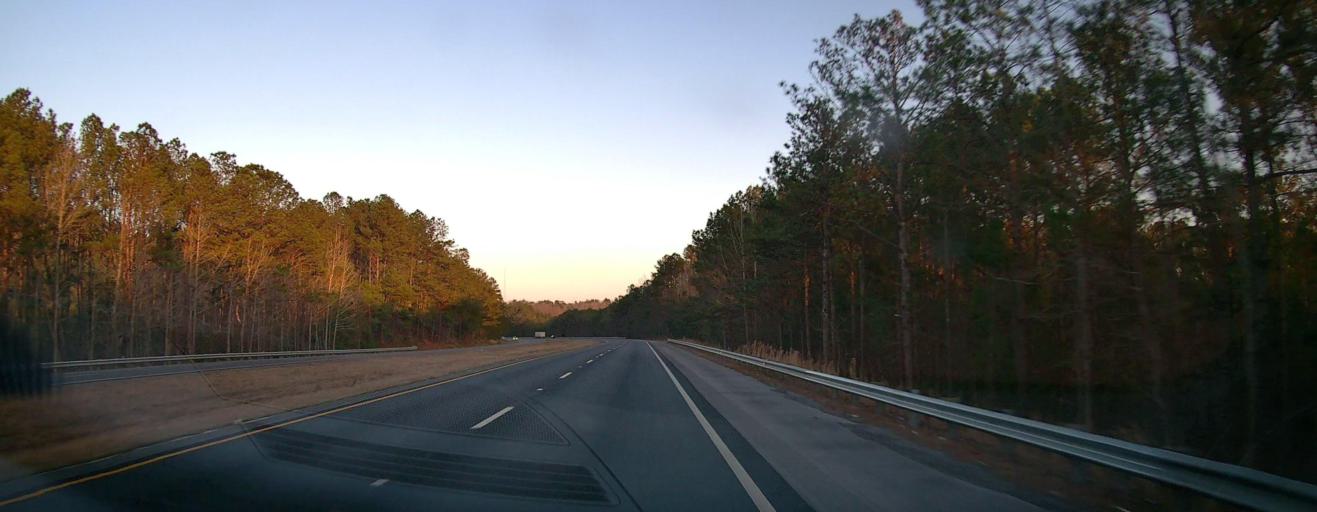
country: US
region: Alabama
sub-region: Coosa County
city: Stewartville
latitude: 33.0768
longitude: -86.1821
